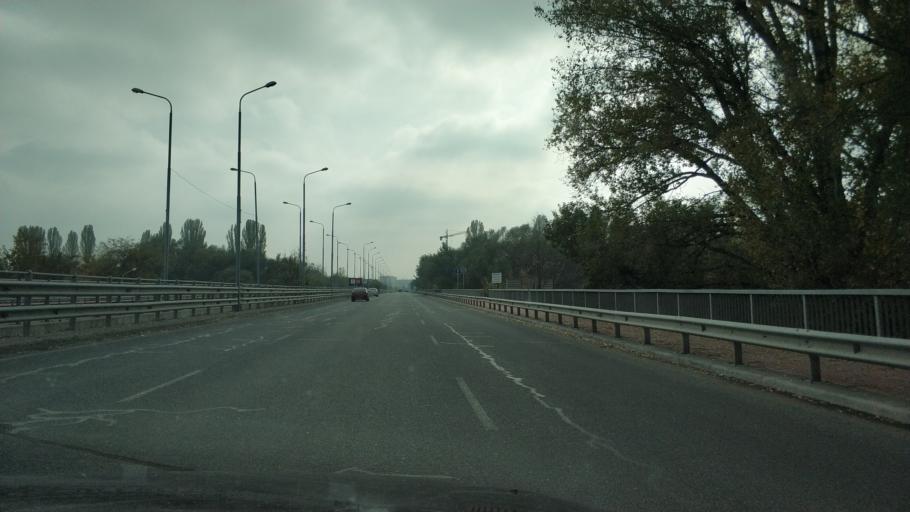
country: BG
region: Plovdiv
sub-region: Obshtina Plovdiv
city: Plovdiv
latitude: 42.1582
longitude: 24.7650
